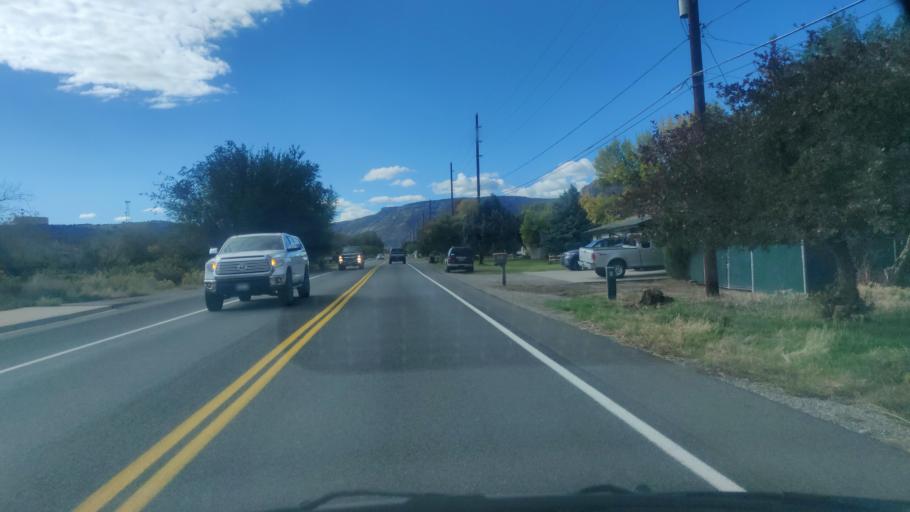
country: US
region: Colorado
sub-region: Mesa County
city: Redlands
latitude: 39.0710
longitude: -108.6449
